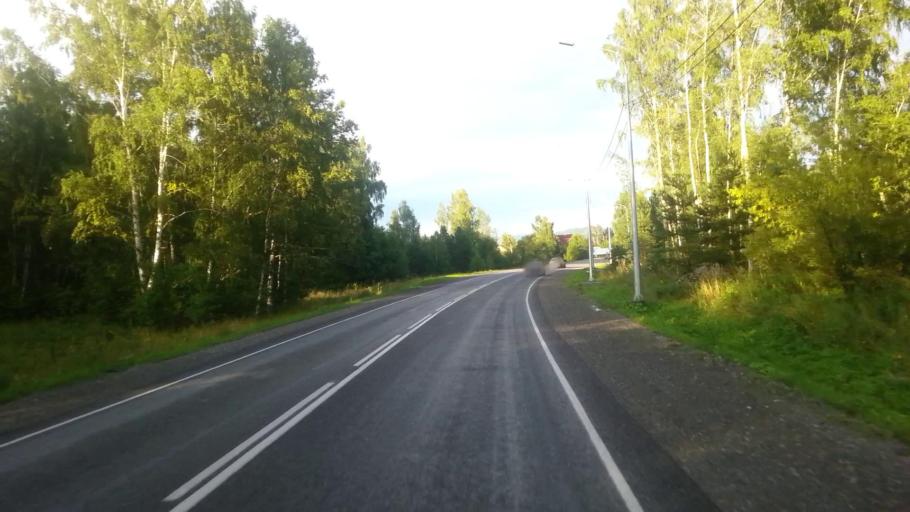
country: RU
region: Altay
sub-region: Mayminskiy Rayon
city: Manzherok
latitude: 51.8686
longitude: 85.7758
